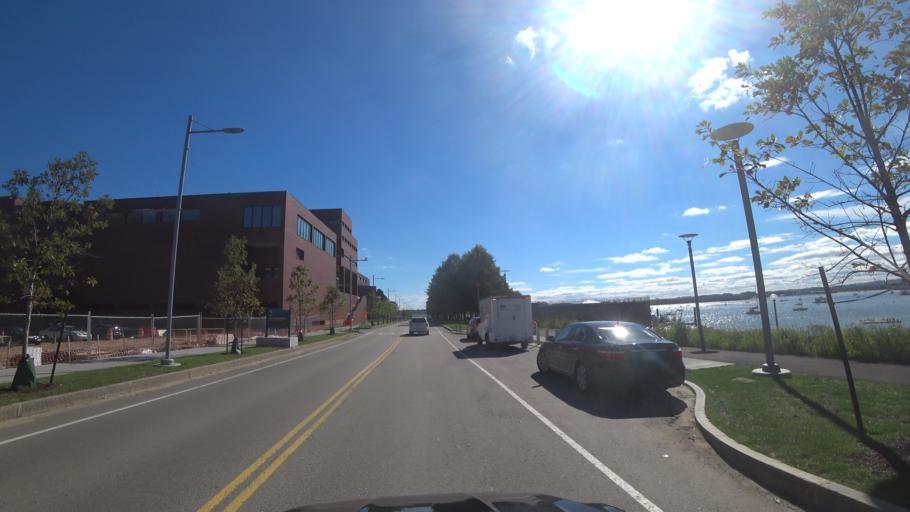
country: US
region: Massachusetts
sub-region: Suffolk County
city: South Boston
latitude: 42.3128
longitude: -71.0411
